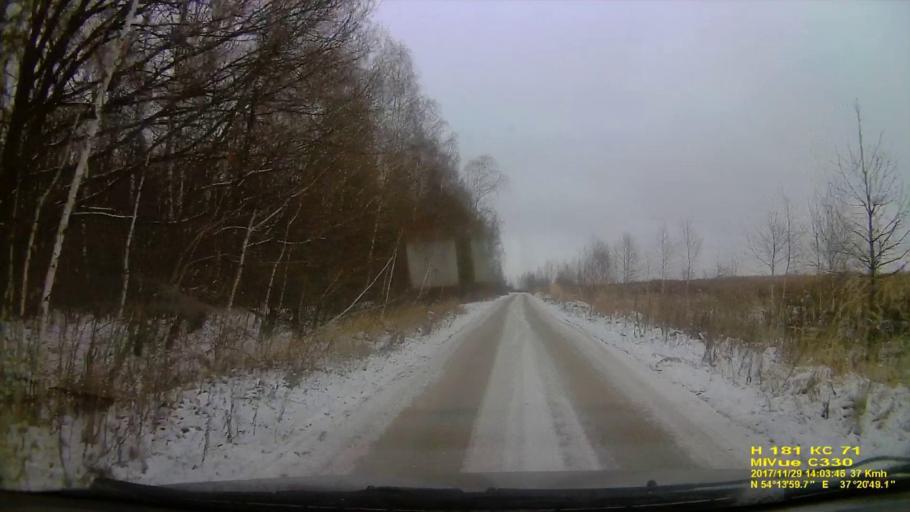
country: RU
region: Tula
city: Leninskiy
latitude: 54.2332
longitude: 37.3471
